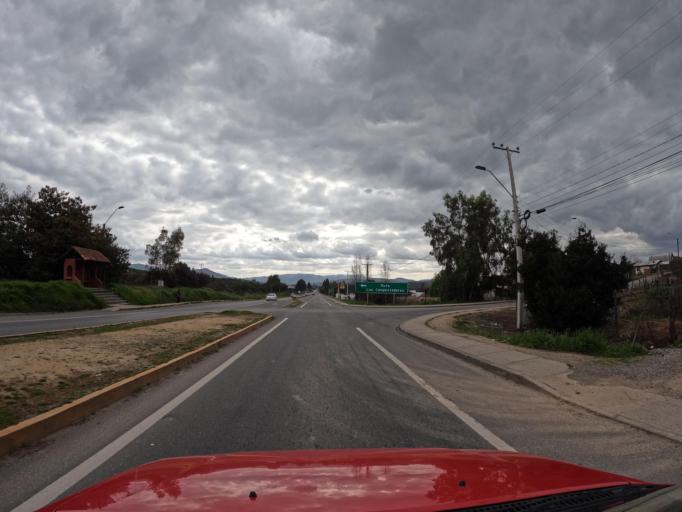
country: CL
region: Maule
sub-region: Provincia de Linares
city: San Javier
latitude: -35.6170
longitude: -71.7780
